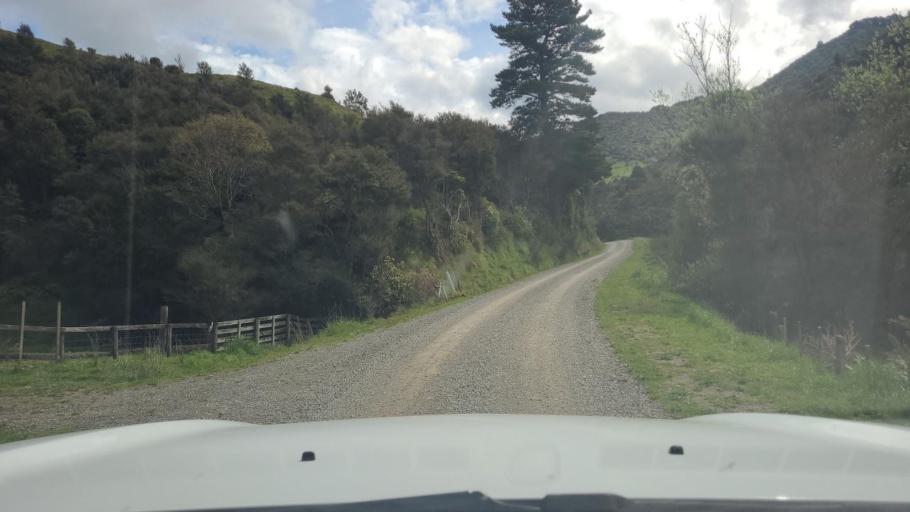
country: NZ
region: Wellington
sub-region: Masterton District
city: Masterton
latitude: -40.9348
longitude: 175.4873
